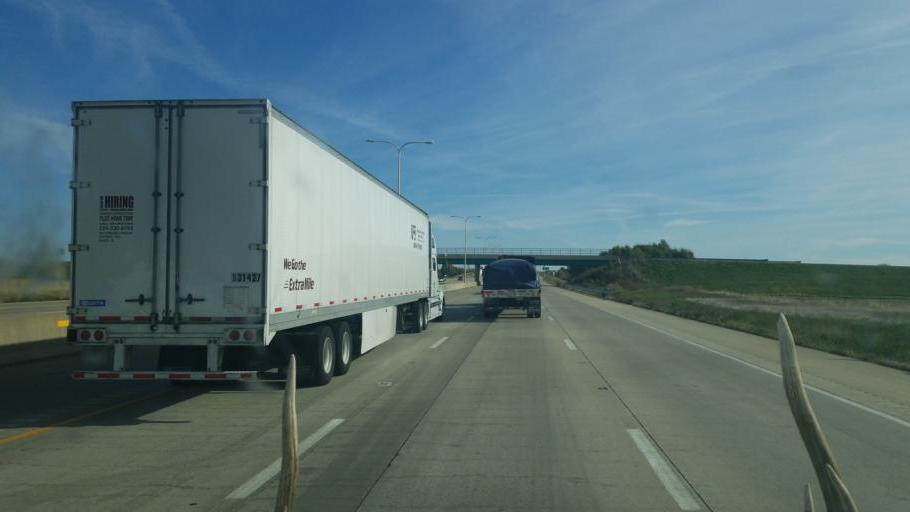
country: US
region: Illinois
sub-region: Effingham County
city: Effingham
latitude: 39.1434
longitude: -88.5441
